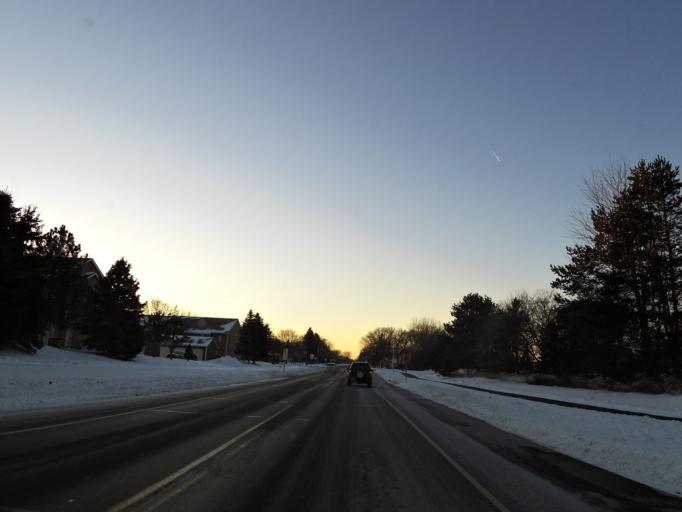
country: US
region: Minnesota
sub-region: Dakota County
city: Rosemount
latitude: 44.7392
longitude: -93.1444
